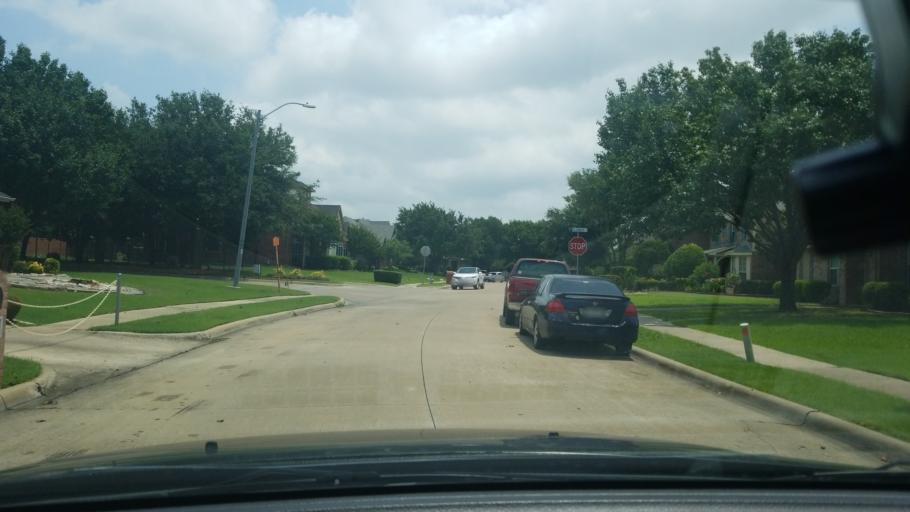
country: US
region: Texas
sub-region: Dallas County
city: Sunnyvale
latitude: 32.8134
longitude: -96.6030
